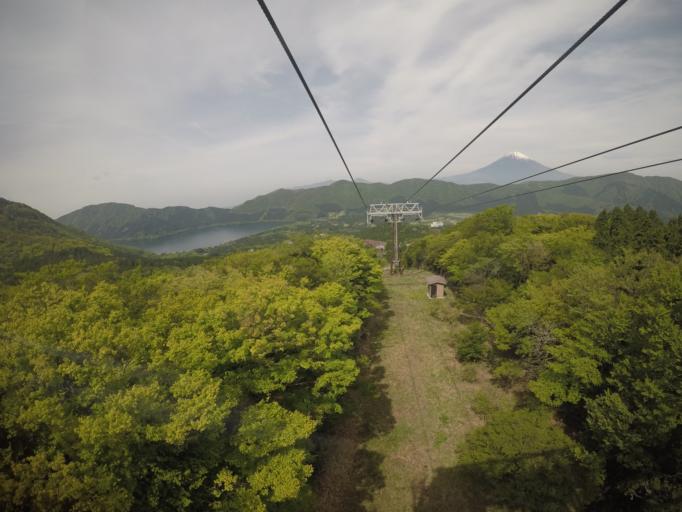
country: JP
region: Kanagawa
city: Hakone
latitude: 35.2444
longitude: 139.0122
